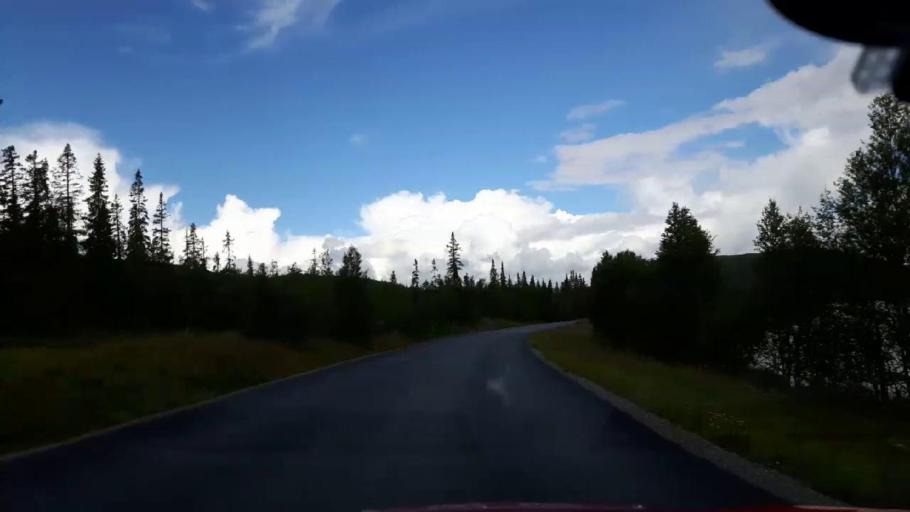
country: SE
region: Vaesterbotten
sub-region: Vilhelmina Kommun
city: Sjoberg
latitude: 65.0114
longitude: 15.1747
